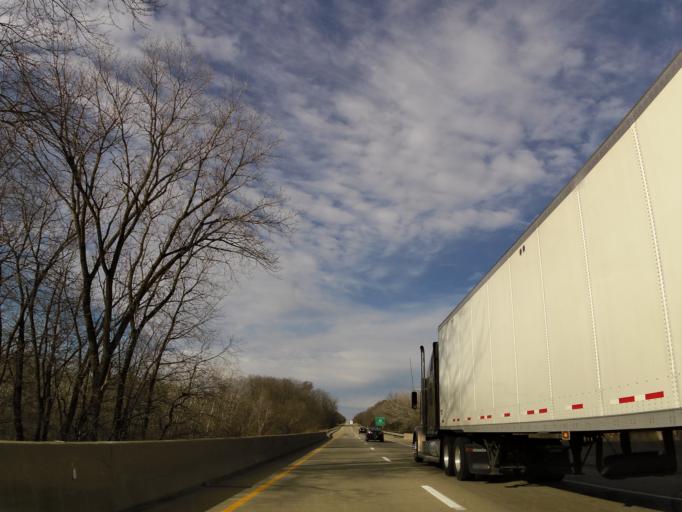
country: US
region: Illinois
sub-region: Woodford County
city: Eureka
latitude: 40.6153
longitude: -89.2515
